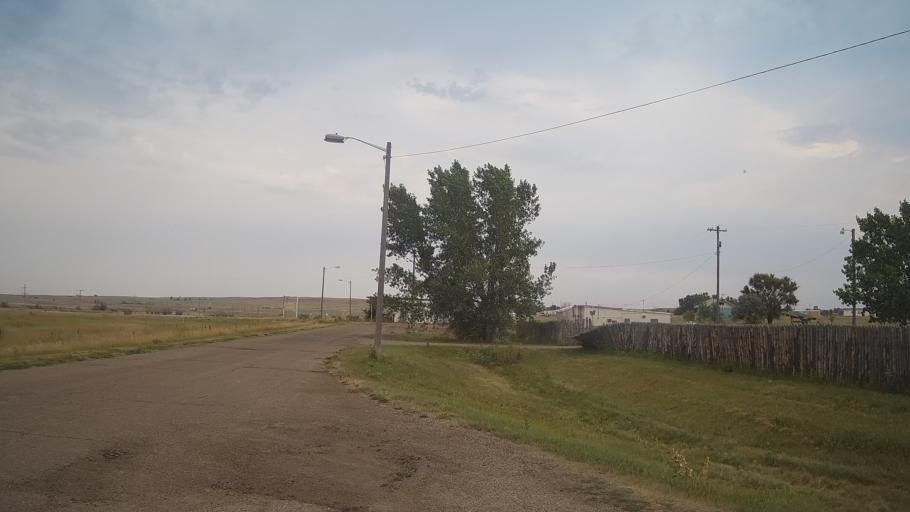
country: US
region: Montana
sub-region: Blaine County
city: Fort Belknap Agency
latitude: 48.4808
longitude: -108.7549
